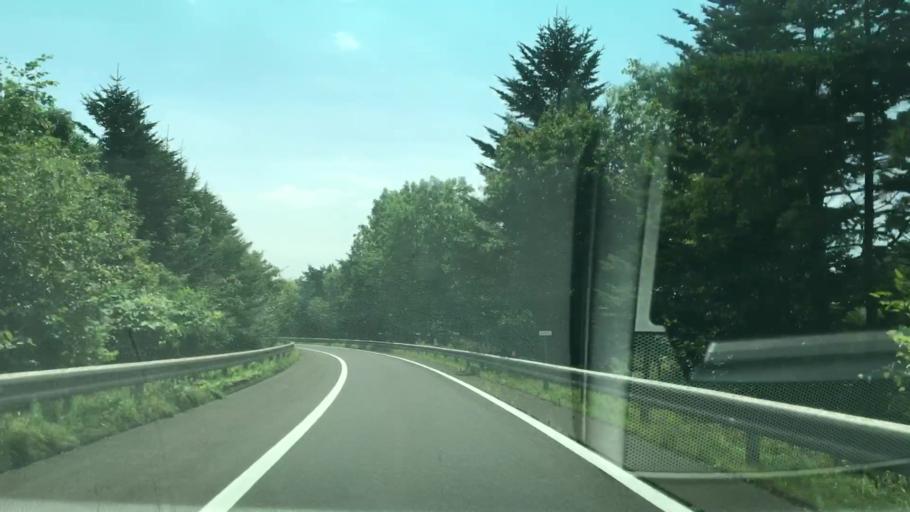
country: JP
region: Hokkaido
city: Muroran
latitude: 42.3999
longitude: 141.0812
